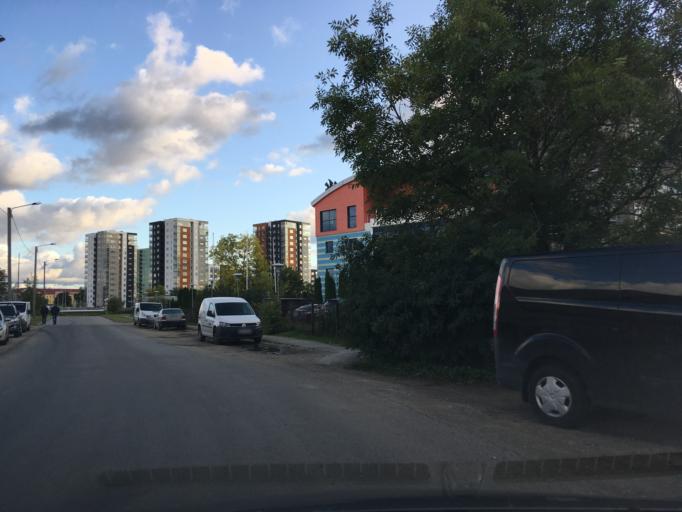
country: EE
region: Harju
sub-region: Tallinna linn
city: Tallinn
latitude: 59.4378
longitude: 24.8080
